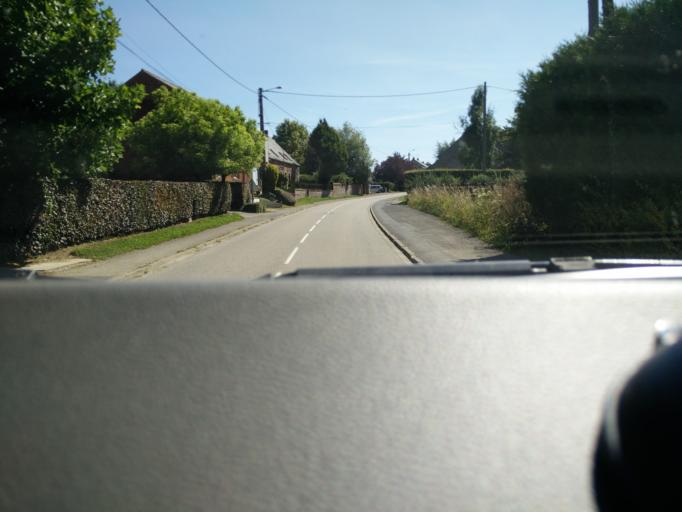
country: FR
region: Nord-Pas-de-Calais
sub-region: Departement du Nord
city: Avesnelles
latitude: 50.1766
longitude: 3.9457
